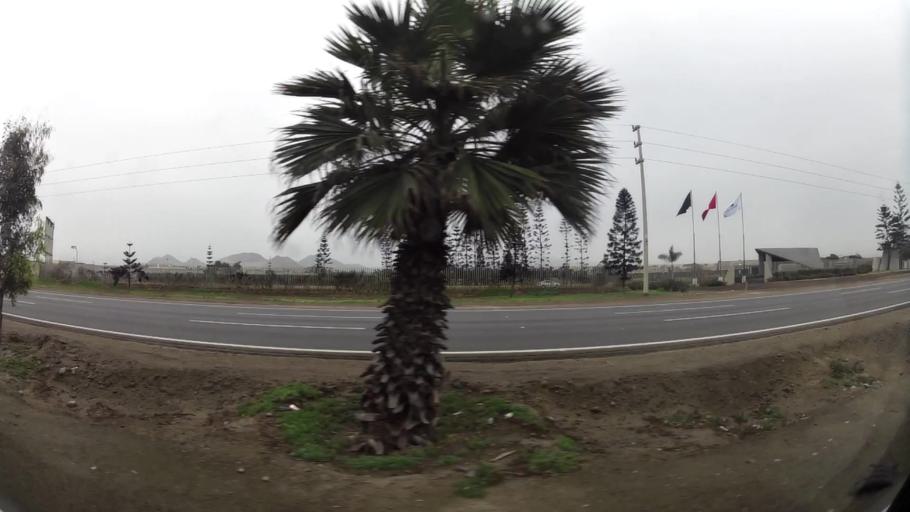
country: PE
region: Lima
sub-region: Lima
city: Punta Hermosa
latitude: -12.2880
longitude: -76.8709
